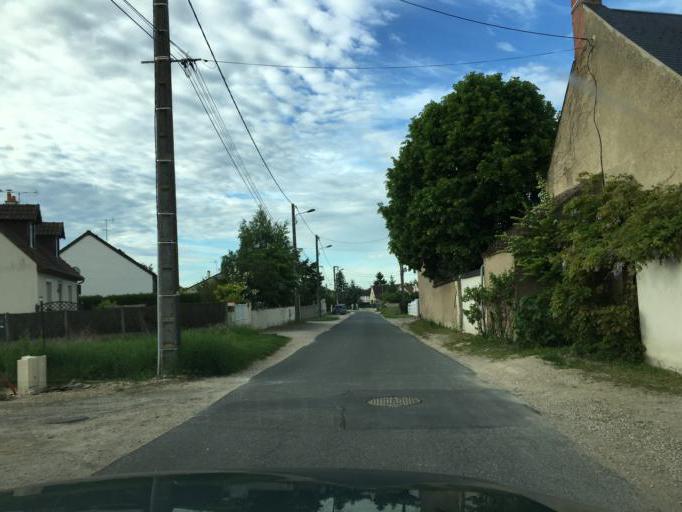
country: FR
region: Centre
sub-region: Departement du Loiret
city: Chaingy
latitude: 47.8886
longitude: 1.7782
